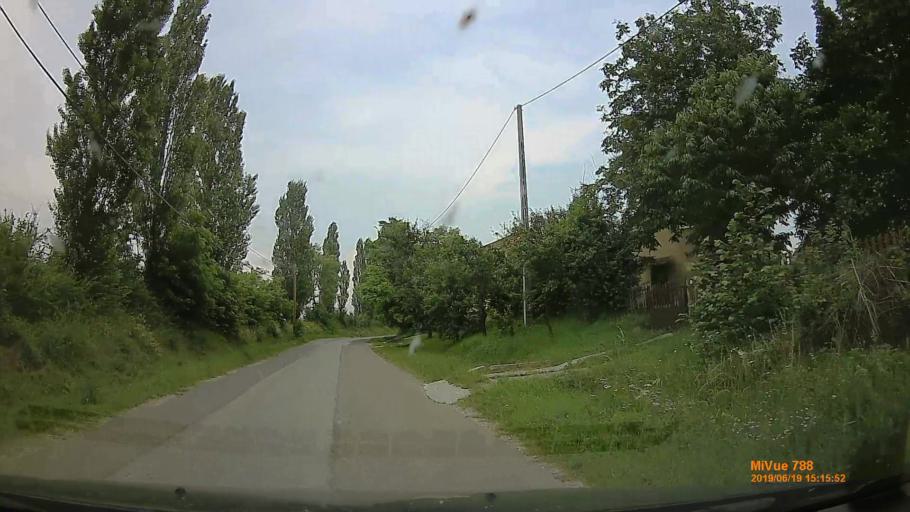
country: HU
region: Baranya
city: Szigetvar
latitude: 46.0749
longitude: 17.8371
